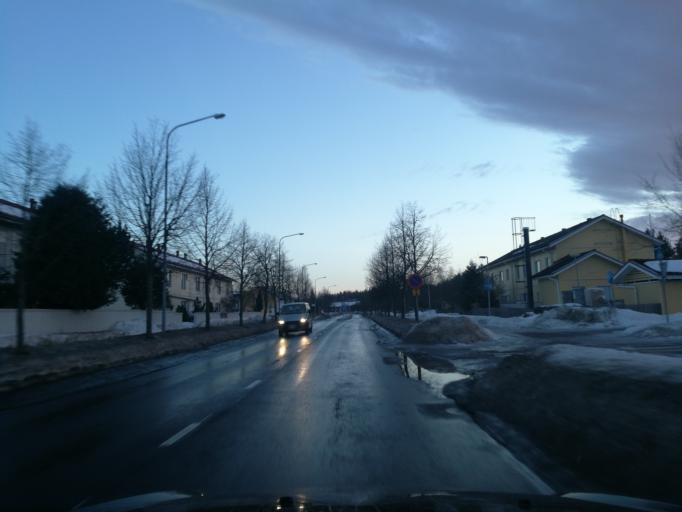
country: FI
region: Uusimaa
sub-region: Helsinki
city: Kerava
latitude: 60.3913
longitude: 25.1463
